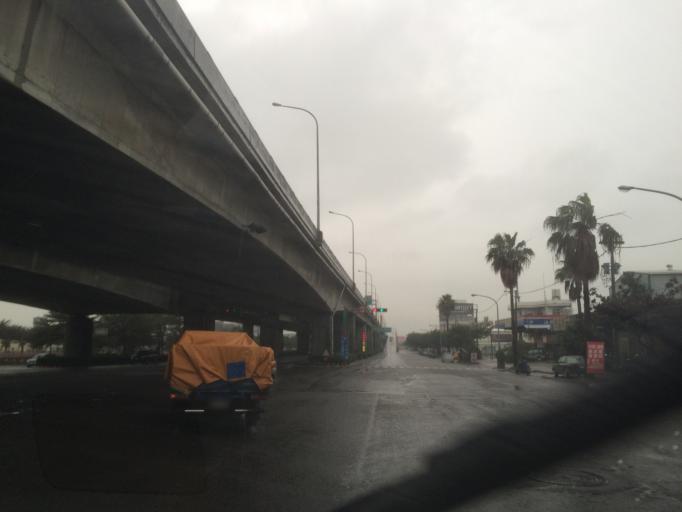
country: TW
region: Taiwan
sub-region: Taichung City
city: Taichung
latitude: 24.1633
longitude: 120.6288
